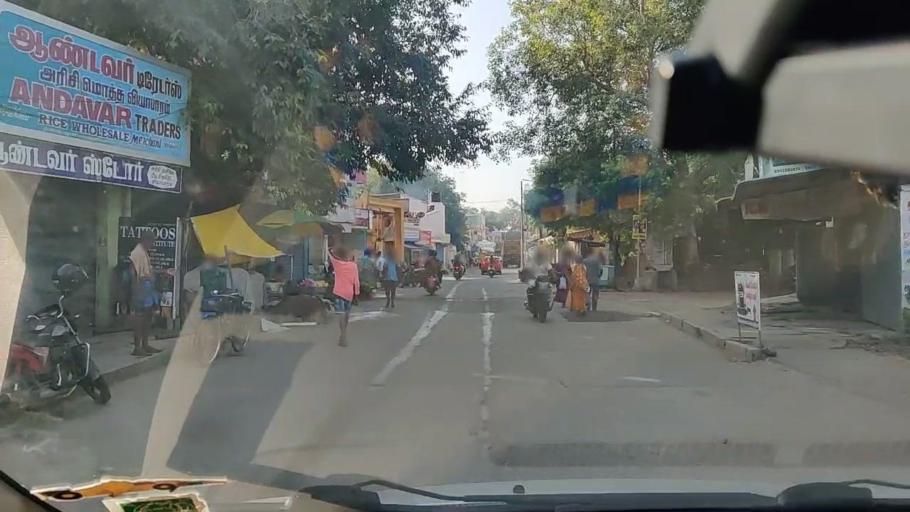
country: IN
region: Tamil Nadu
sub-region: Chennai
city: George Town
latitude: 13.1160
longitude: 80.2629
